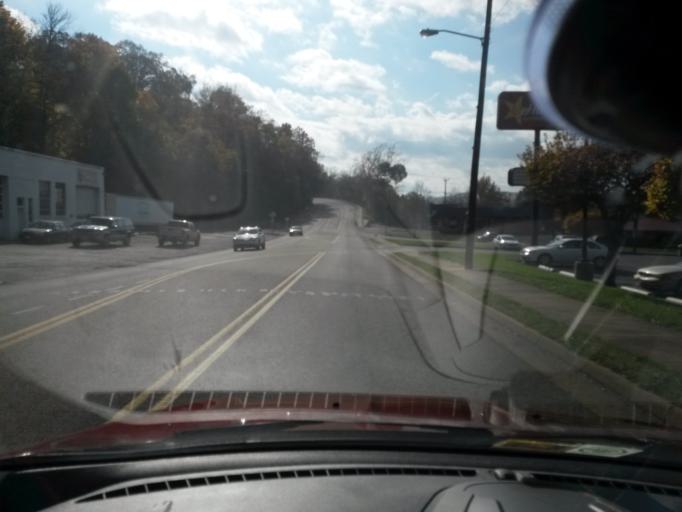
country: US
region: Virginia
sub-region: City of Covington
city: Fairlawn
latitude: 37.7819
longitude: -79.9860
